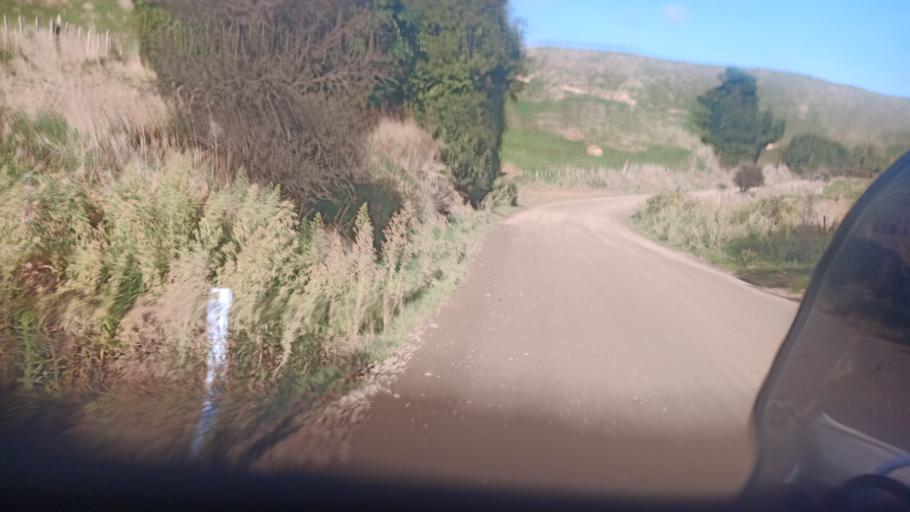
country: NZ
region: Bay of Plenty
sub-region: Opotiki District
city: Opotiki
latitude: -38.4379
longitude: 177.5435
